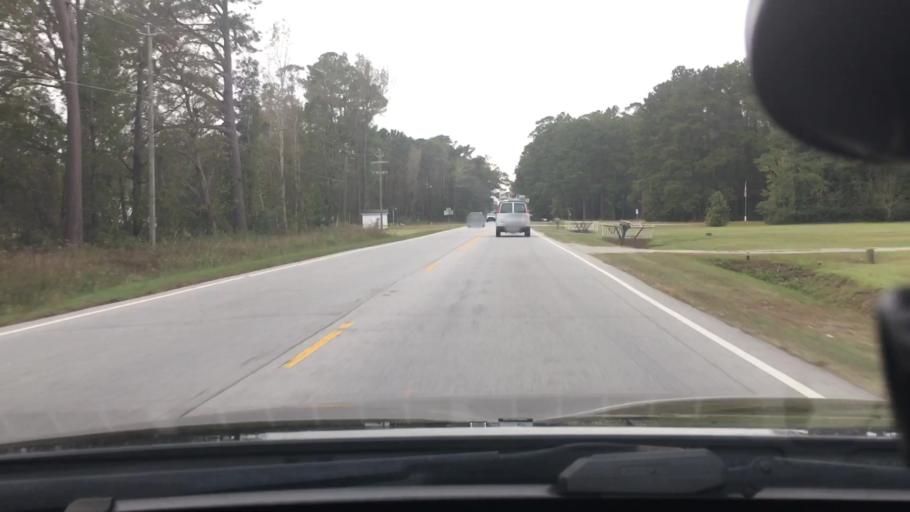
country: US
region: North Carolina
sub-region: Craven County
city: Vanceboro
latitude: 35.2611
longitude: -77.1014
